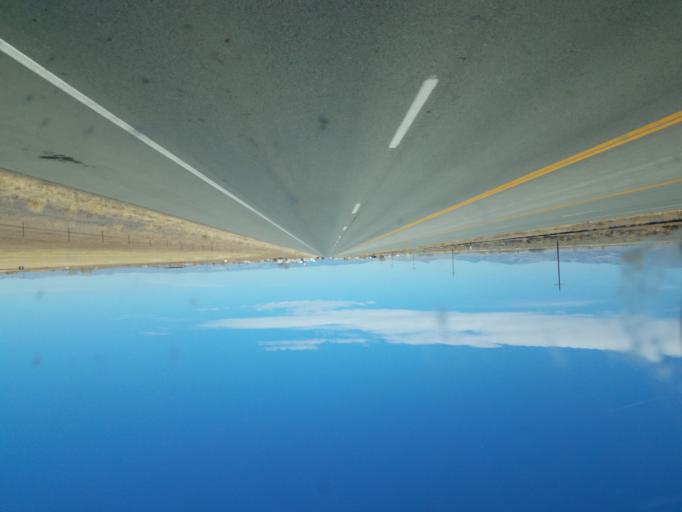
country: US
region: Colorado
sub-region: Rio Grande County
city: Monte Vista
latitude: 37.5259
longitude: -106.0142
